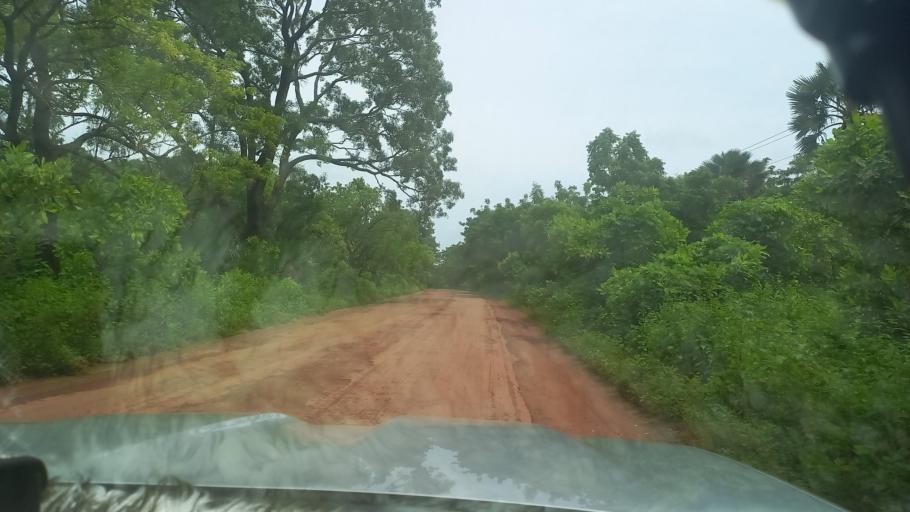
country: SN
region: Kolda
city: Marsassoum
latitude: 12.9062
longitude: -16.0163
